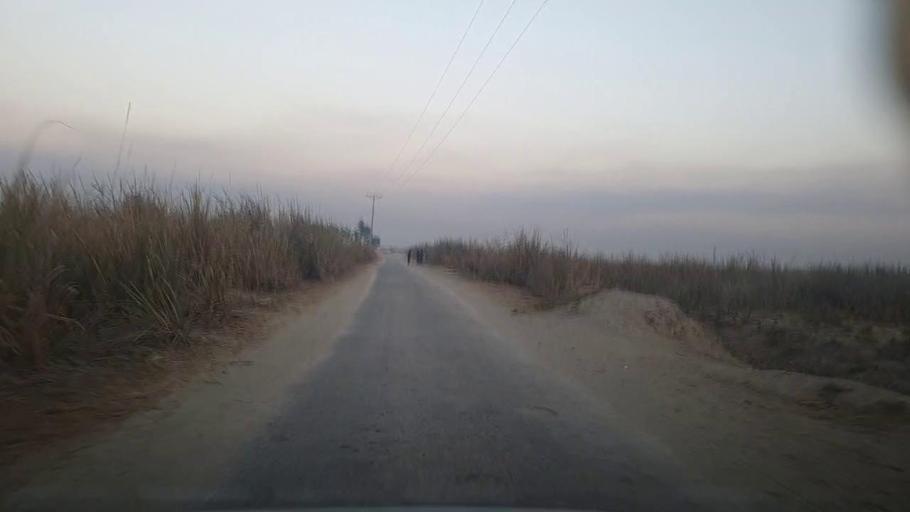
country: PK
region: Sindh
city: Kandiari
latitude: 26.6864
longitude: 68.9211
